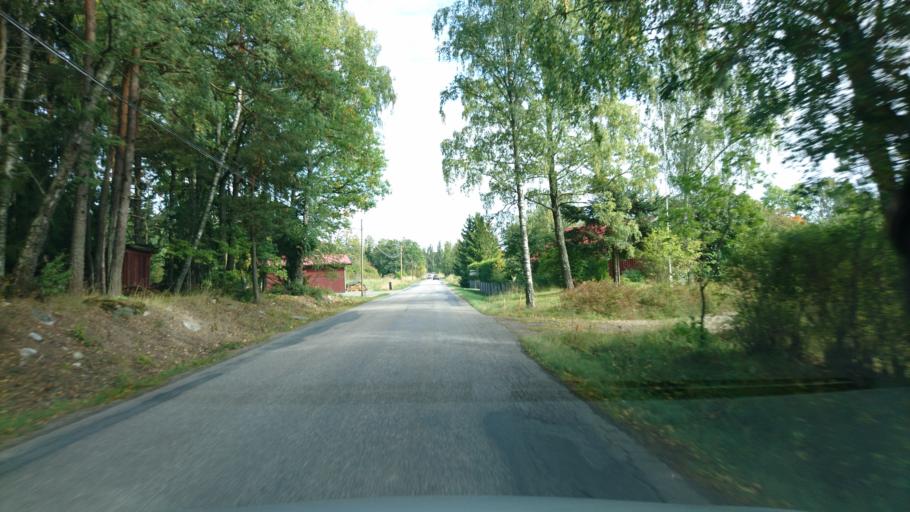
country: SE
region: Soedermanland
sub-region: Strangnas Kommun
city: Stallarholmen
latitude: 59.3710
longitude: 17.2474
